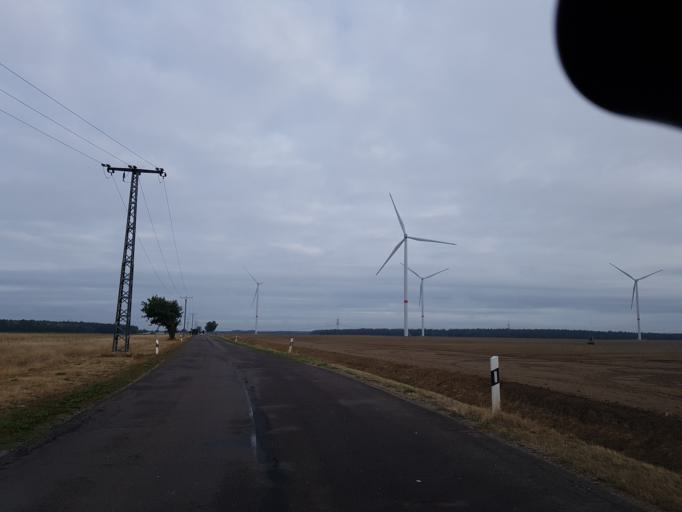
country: DE
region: Saxony-Anhalt
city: Klieken
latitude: 51.9311
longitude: 12.3237
